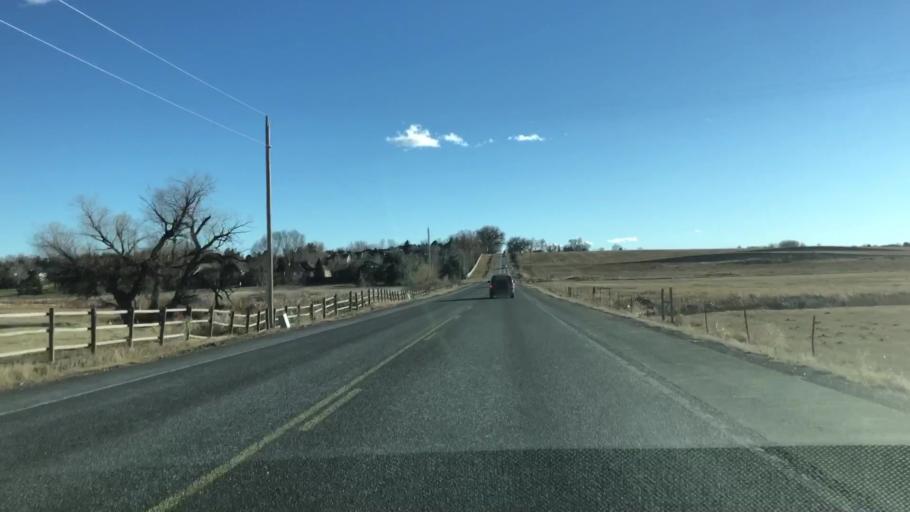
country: US
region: Colorado
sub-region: Weld County
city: Windsor
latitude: 40.4890
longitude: -104.9820
